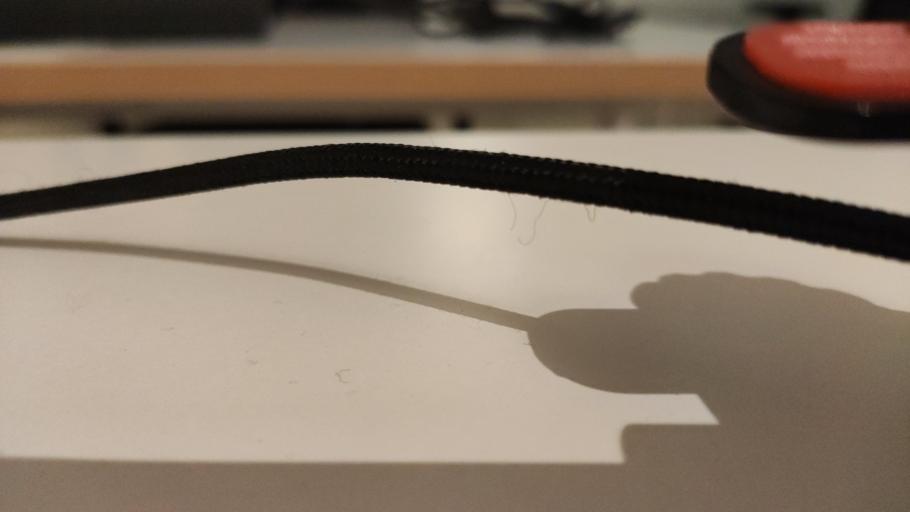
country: RU
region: Moskovskaya
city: Semkhoz
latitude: 56.3902
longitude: 38.0466
